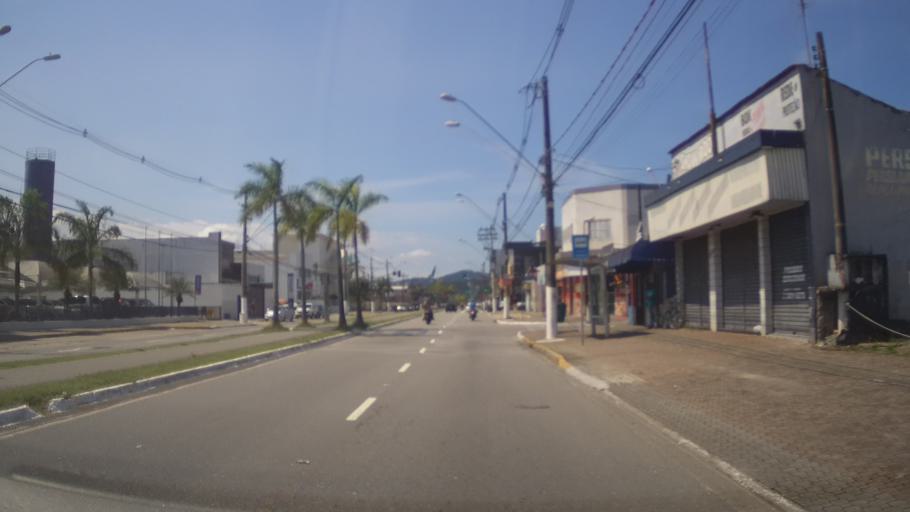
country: BR
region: Sao Paulo
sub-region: Praia Grande
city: Praia Grande
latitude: -24.0088
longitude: -46.4342
